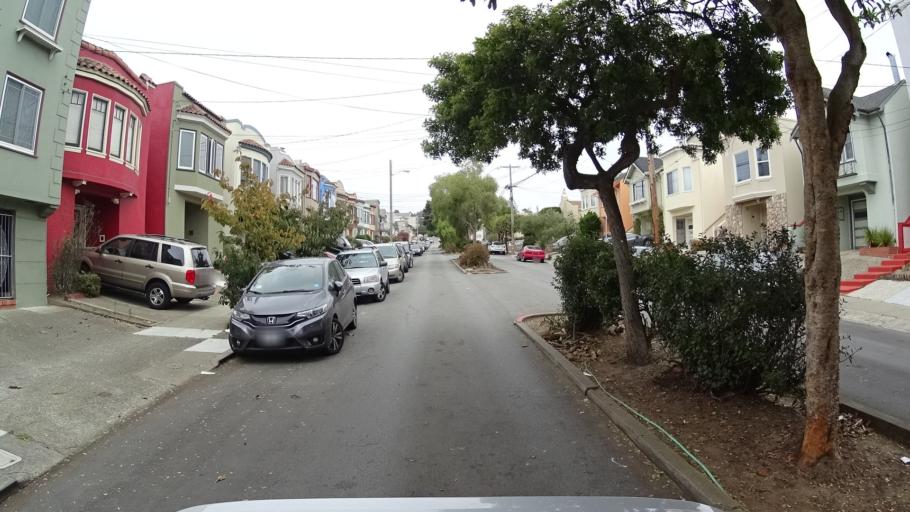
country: US
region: California
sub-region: San Mateo County
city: Daly City
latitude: 37.7759
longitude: -122.4995
